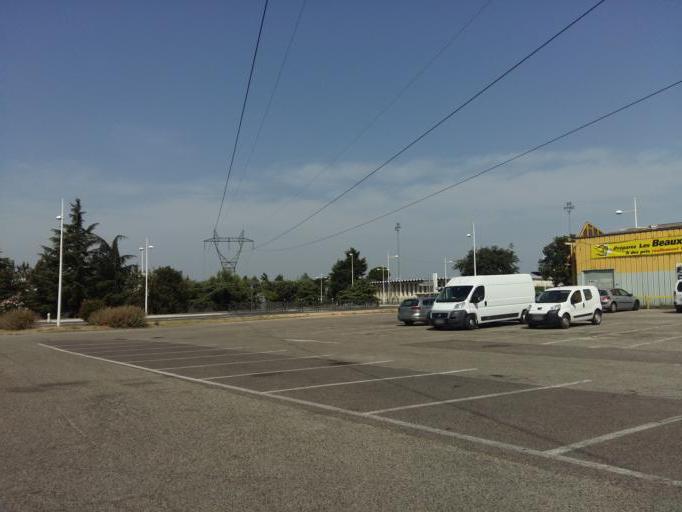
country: FR
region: Provence-Alpes-Cote d'Azur
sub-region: Departement du Vaucluse
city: Bollene
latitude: 44.2926
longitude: 4.7539
